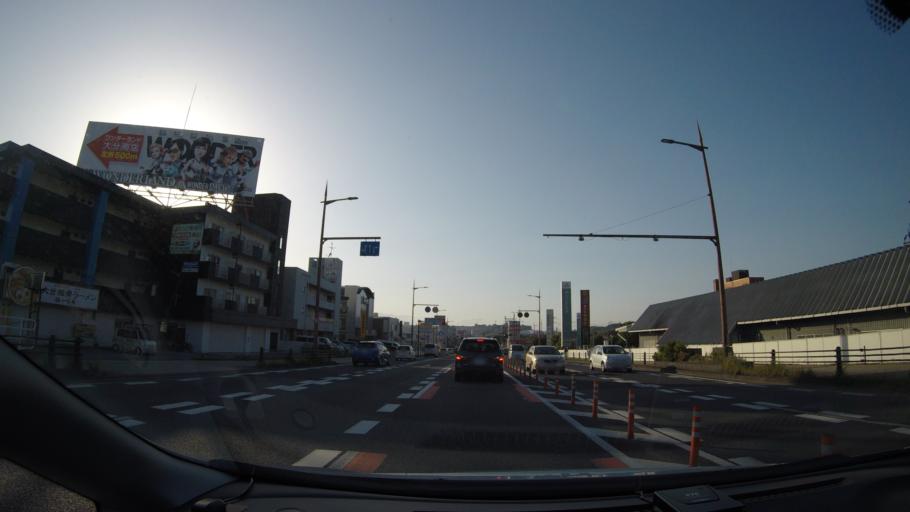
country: JP
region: Oita
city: Oita
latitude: 33.2041
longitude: 131.6041
